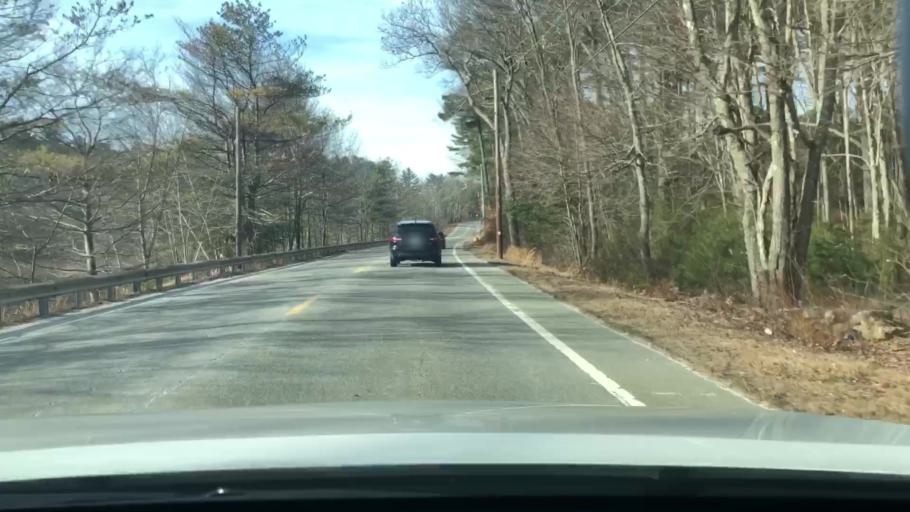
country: US
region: Massachusetts
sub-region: Worcester County
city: Northbridge
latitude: 42.1813
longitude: -71.6431
